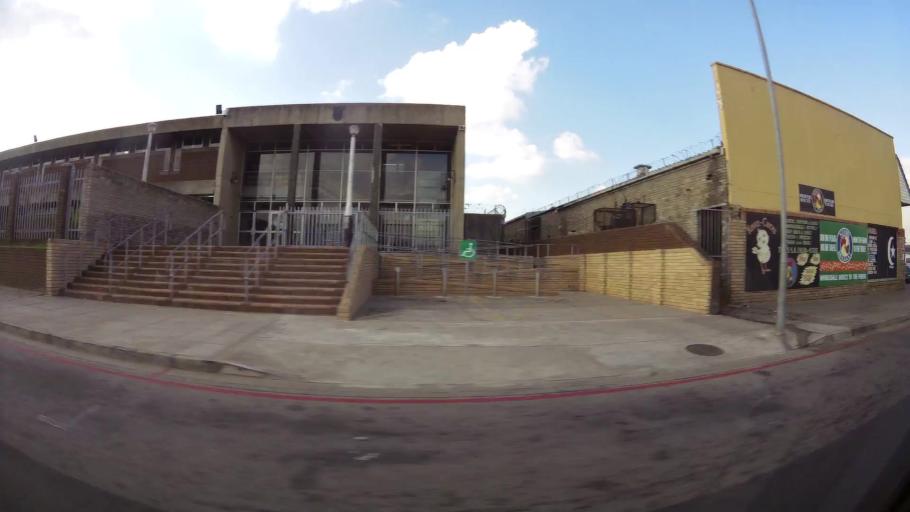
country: ZA
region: Eastern Cape
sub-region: Nelson Mandela Bay Metropolitan Municipality
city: Uitenhage
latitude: -33.7720
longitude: 25.3999
